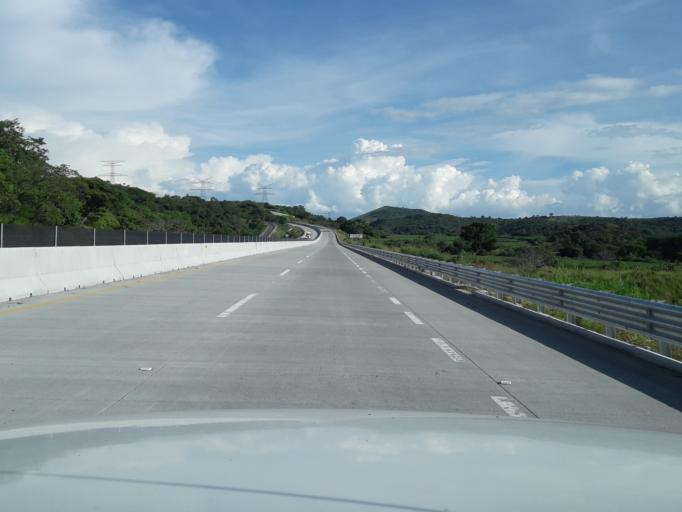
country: MX
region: Jalisco
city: Tala
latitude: 20.5915
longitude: -103.6710
